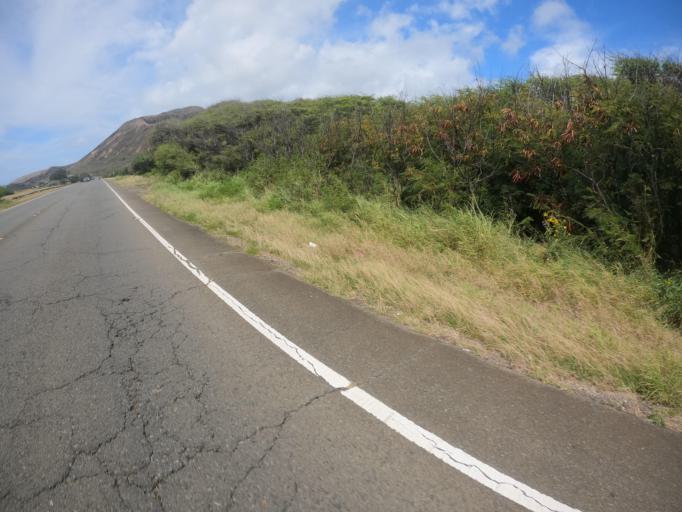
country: US
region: Hawaii
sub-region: Honolulu County
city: Waimanalo Beach
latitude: 21.2886
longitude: -157.6694
